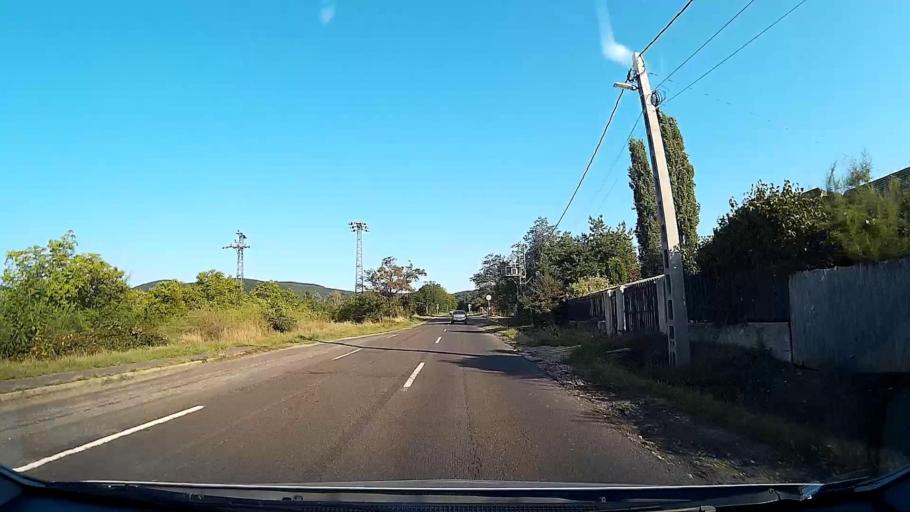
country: HU
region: Pest
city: Szentendre
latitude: 47.6985
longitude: 19.0366
